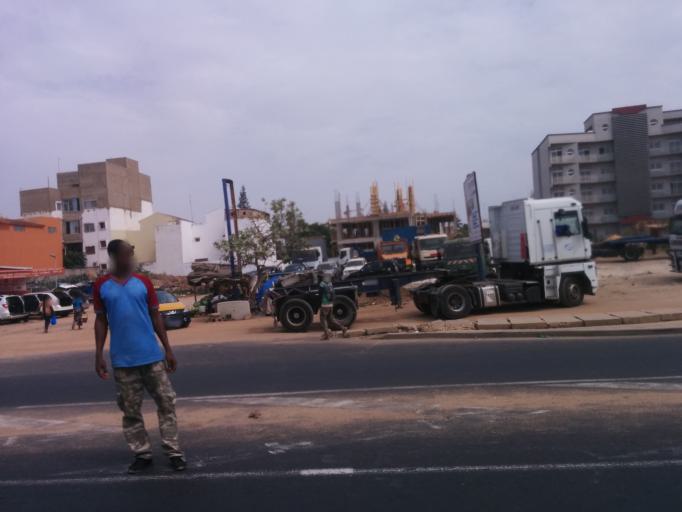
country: SN
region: Dakar
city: Grand Dakar
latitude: 14.7389
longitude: -17.4719
